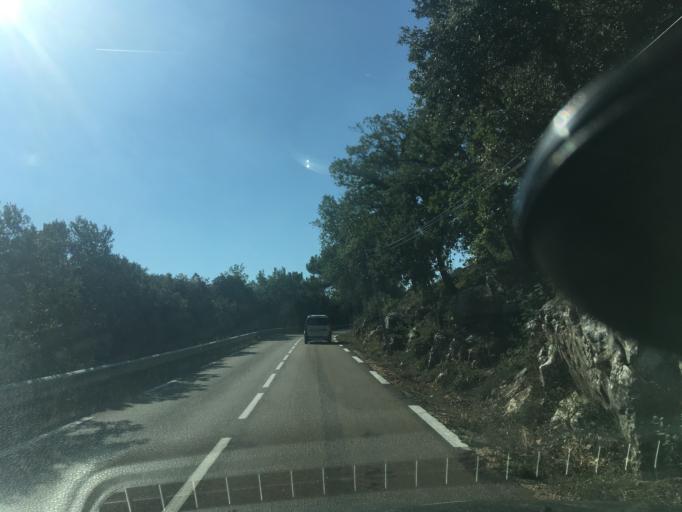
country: FR
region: Provence-Alpes-Cote d'Azur
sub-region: Departement du Var
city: Regusse
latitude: 43.6113
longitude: 6.0687
